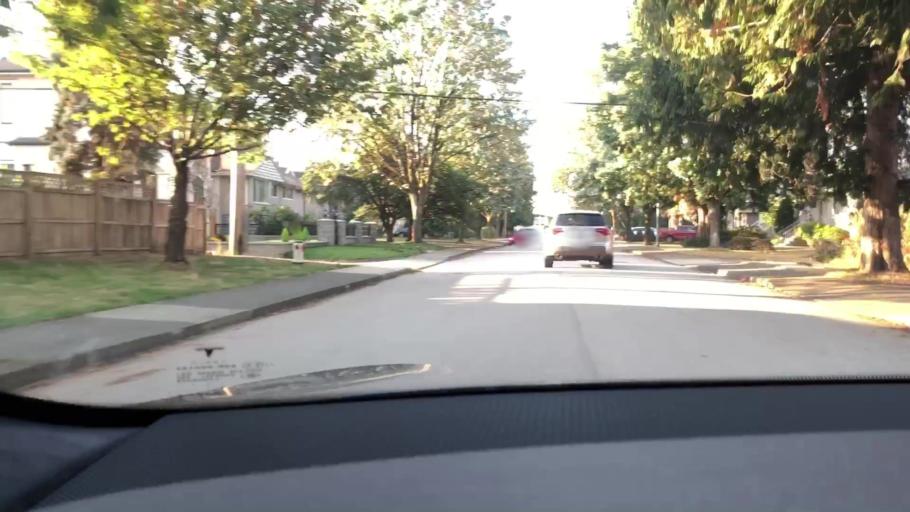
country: CA
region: British Columbia
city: Burnaby
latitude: 49.2238
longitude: -122.9625
